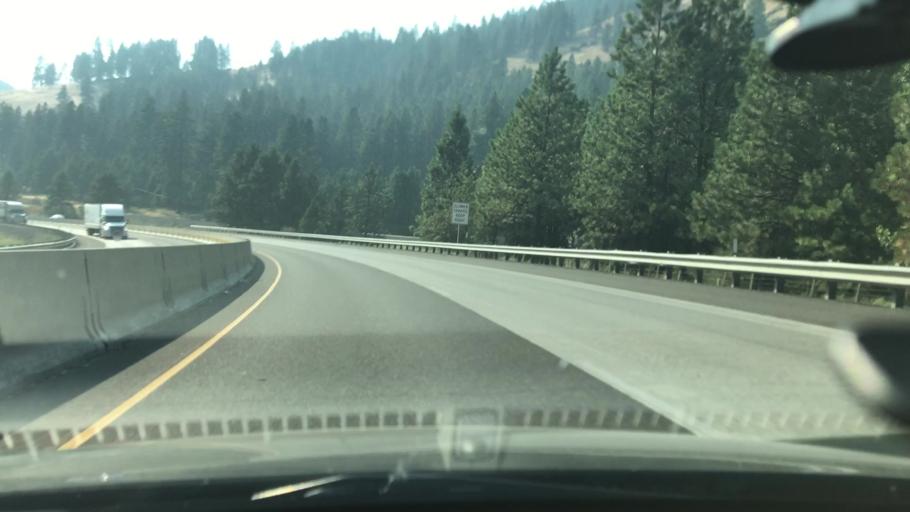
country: US
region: Oregon
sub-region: Union County
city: La Grande
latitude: 45.3546
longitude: -118.1871
